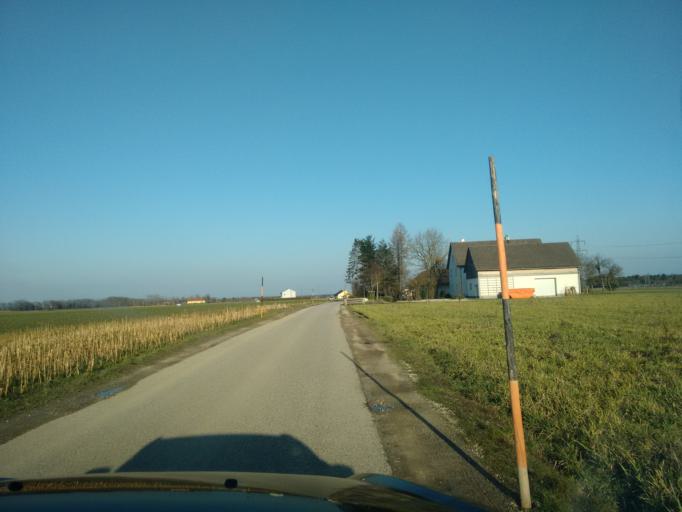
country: AT
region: Upper Austria
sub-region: Wels-Land
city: Marchtrenk
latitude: 48.2040
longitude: 14.1176
